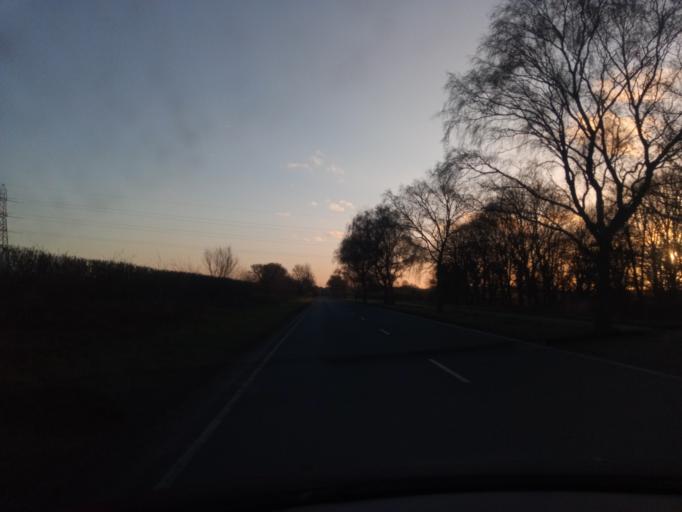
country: GB
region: England
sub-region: Nottinghamshire
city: Farnsfield
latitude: 53.0709
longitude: -1.0697
